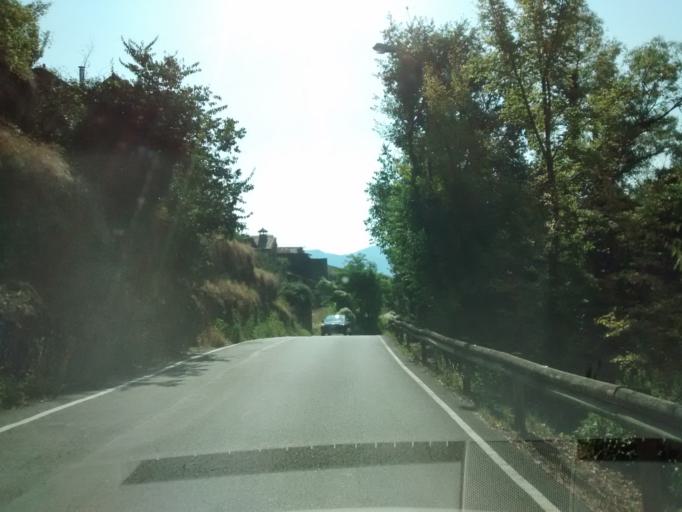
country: ES
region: Aragon
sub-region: Provincia de Huesca
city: Ainsa
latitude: 42.4163
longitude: 0.1388
